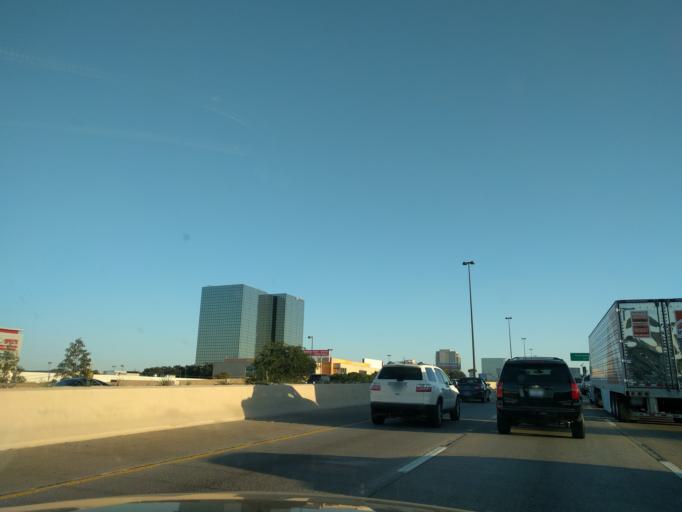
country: US
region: Texas
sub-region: Dallas County
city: University Park
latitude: 32.8793
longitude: -96.7703
